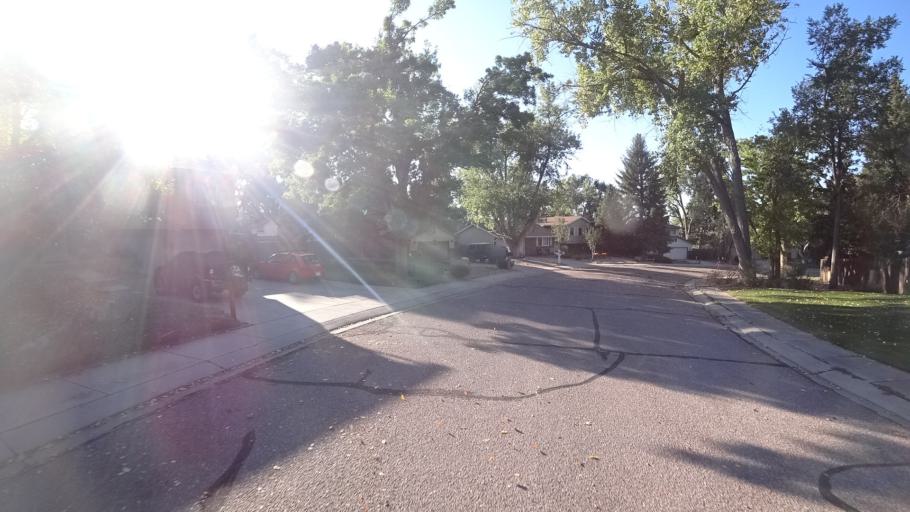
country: US
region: Colorado
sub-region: El Paso County
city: Cimarron Hills
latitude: 38.8807
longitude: -104.7455
